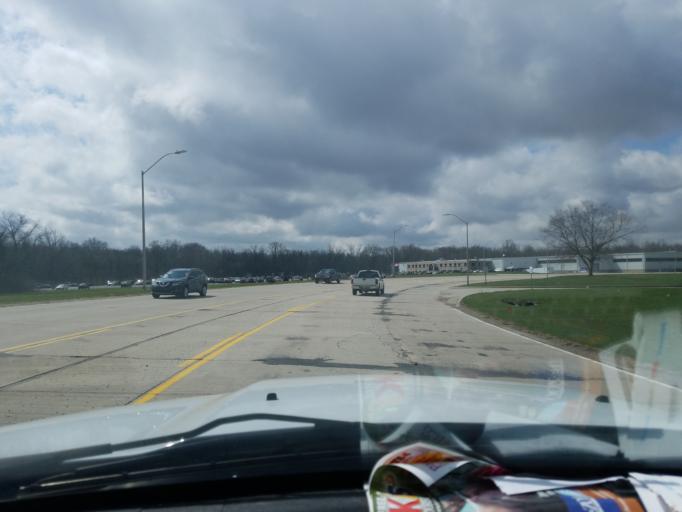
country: US
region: Indiana
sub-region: Sullivan County
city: Farmersburg
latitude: 39.3442
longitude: -87.3905
